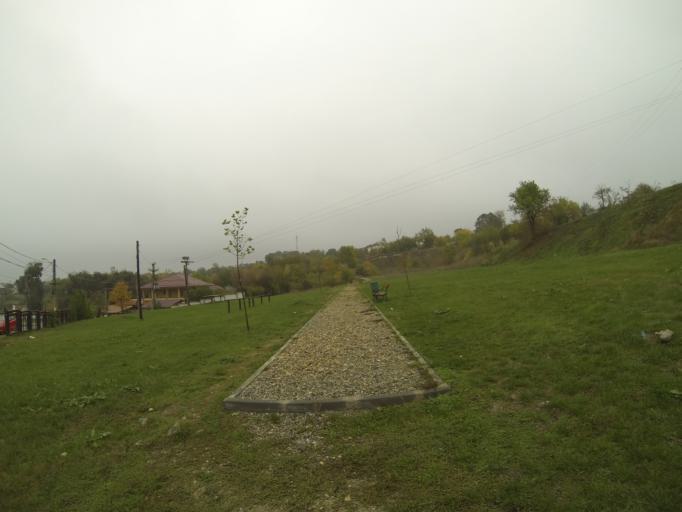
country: RO
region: Dolj
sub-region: Comuna Segarcea
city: Segarcea
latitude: 44.0957
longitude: 23.7431
